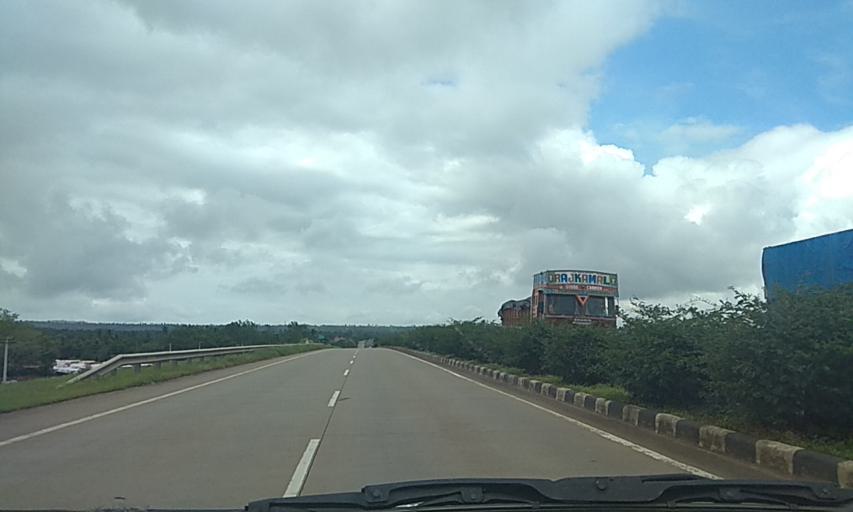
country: IN
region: Karnataka
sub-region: Belgaum
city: Sankeshwar
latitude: 16.3131
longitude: 74.4279
